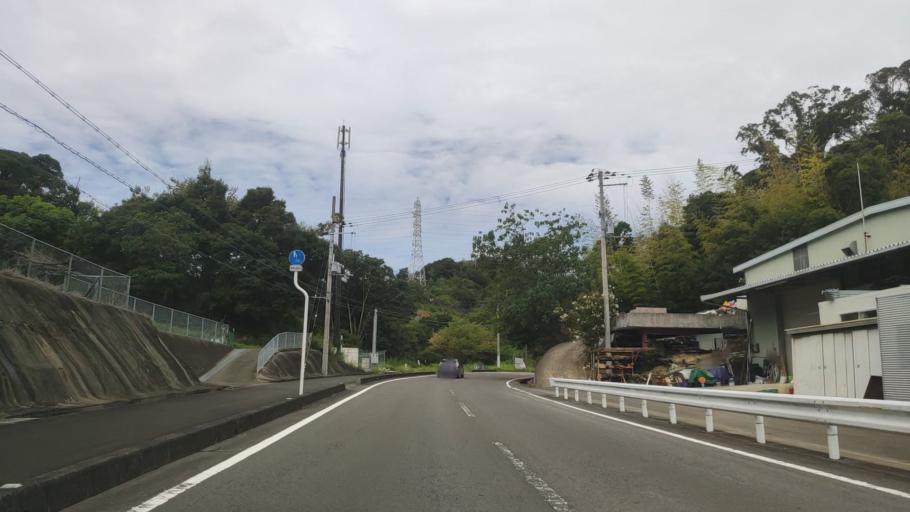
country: JP
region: Wakayama
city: Tanabe
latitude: 33.6837
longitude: 135.3877
